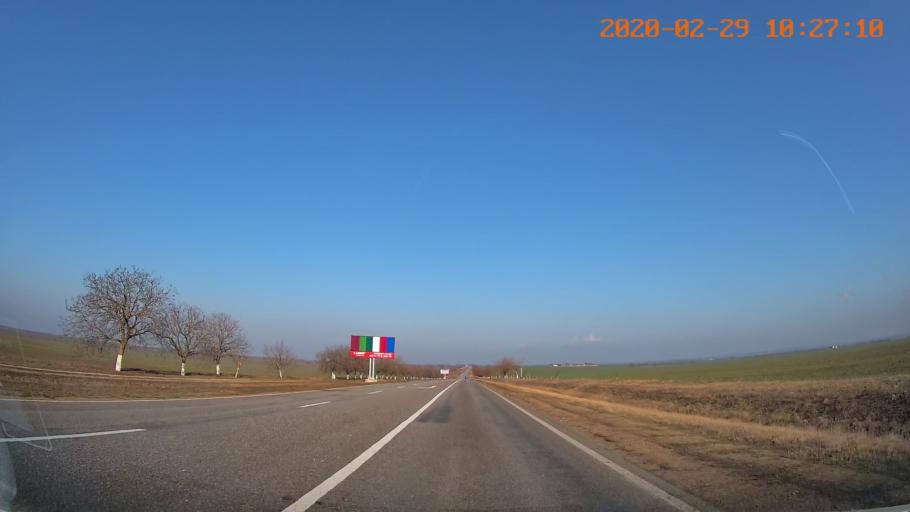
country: MD
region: Telenesti
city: Tiraspolul Nou
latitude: 46.8923
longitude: 29.5994
